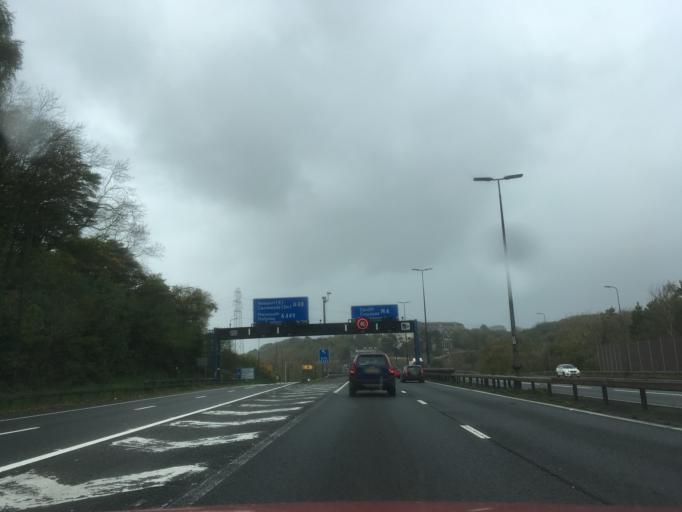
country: GB
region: Wales
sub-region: Newport
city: Langstone
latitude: 51.6016
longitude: -2.9199
